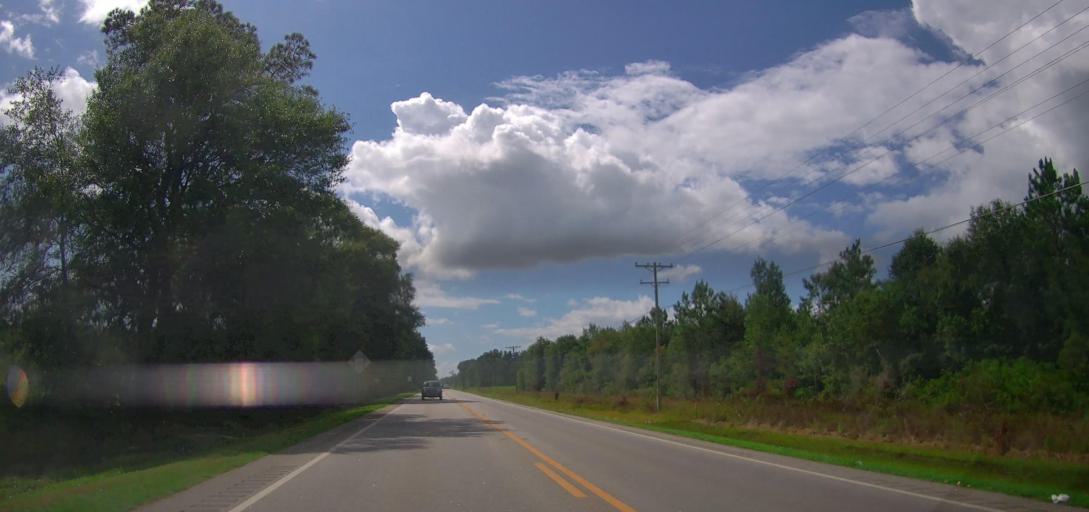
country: US
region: Georgia
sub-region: Coffee County
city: Broxton
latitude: 31.5489
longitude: -82.9488
